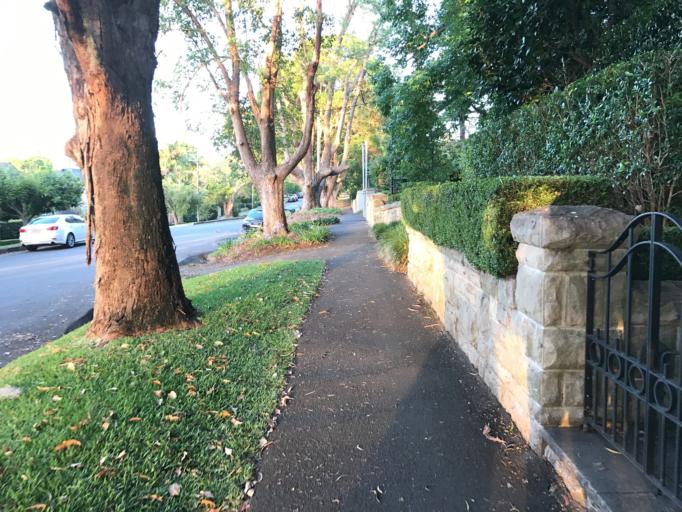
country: AU
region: New South Wales
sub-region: Ku-ring-gai
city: Killara
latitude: -33.7631
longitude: 151.1665
